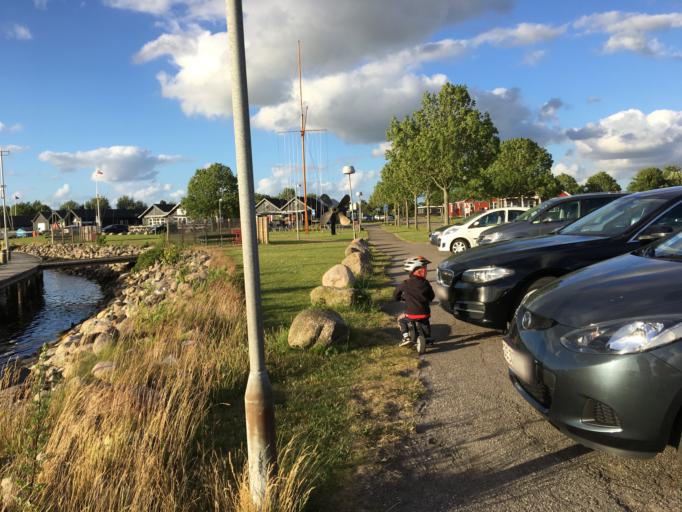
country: DK
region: South Denmark
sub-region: Middelfart Kommune
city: Middelfart
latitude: 55.4904
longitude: 9.7298
